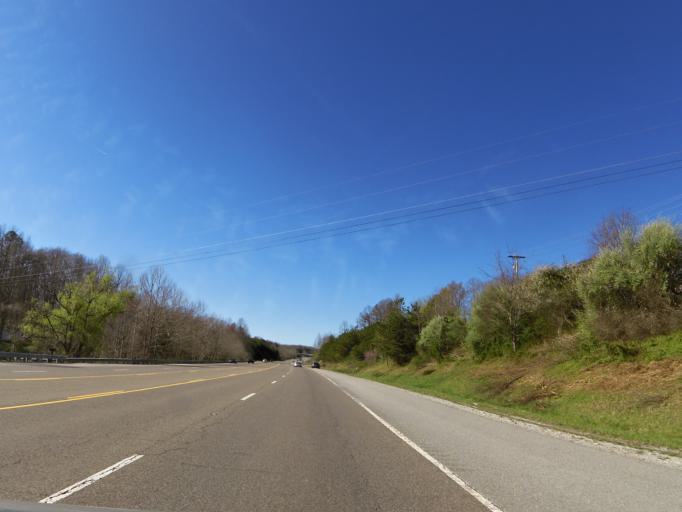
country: US
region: Tennessee
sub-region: Scott County
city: Oneida
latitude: 36.4484
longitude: -84.5420
